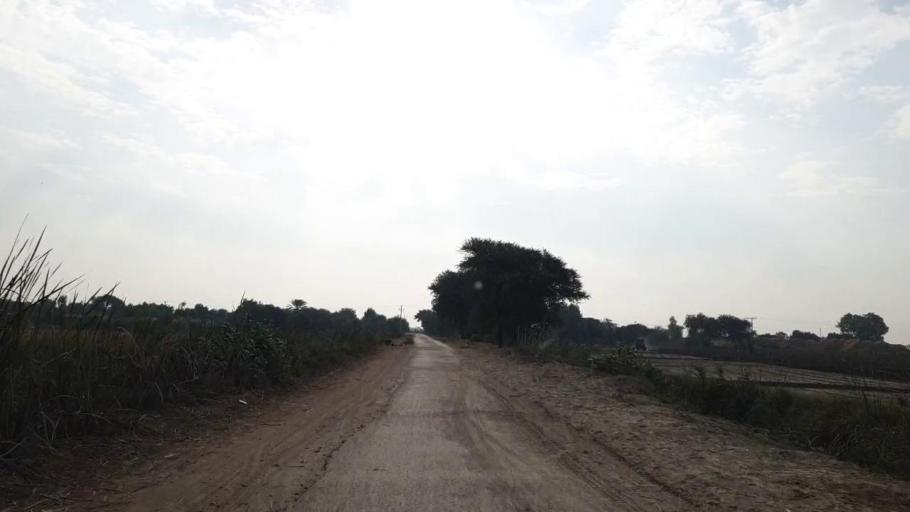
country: PK
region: Sindh
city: Tando Muhammad Khan
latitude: 25.0360
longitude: 68.4363
